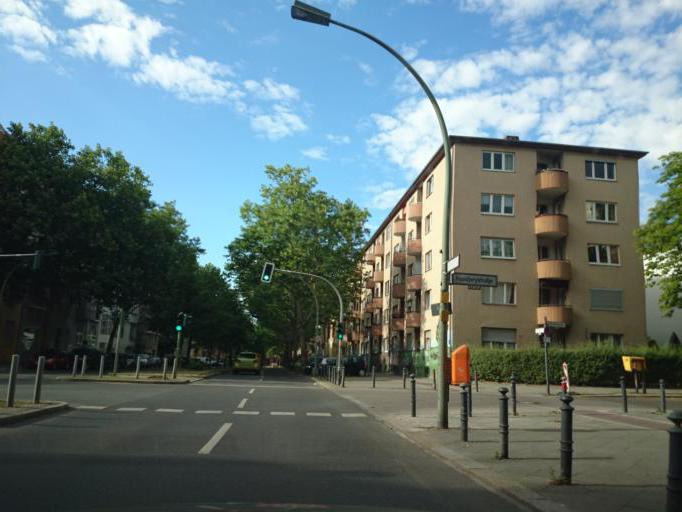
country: DE
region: Berlin
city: Friedenau
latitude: 52.4688
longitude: 13.3282
